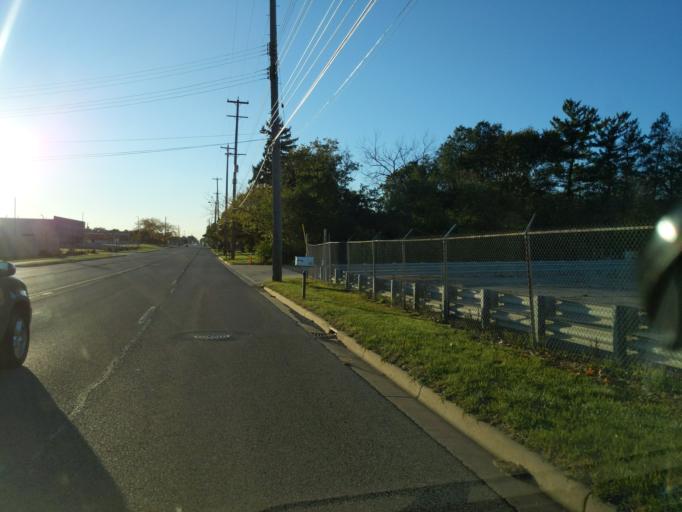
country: US
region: Michigan
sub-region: Ingham County
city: Edgemont Park
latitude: 42.7266
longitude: -84.5864
